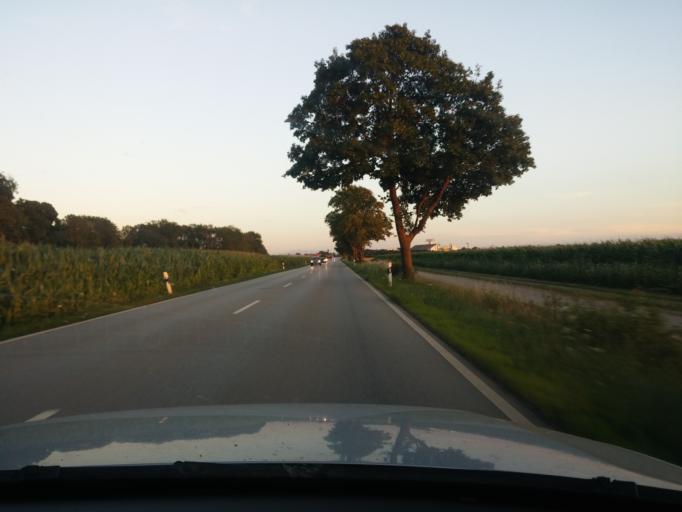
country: DE
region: Bavaria
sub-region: Upper Bavaria
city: Kirchheim bei Muenchen
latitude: 48.1575
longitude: 11.7849
